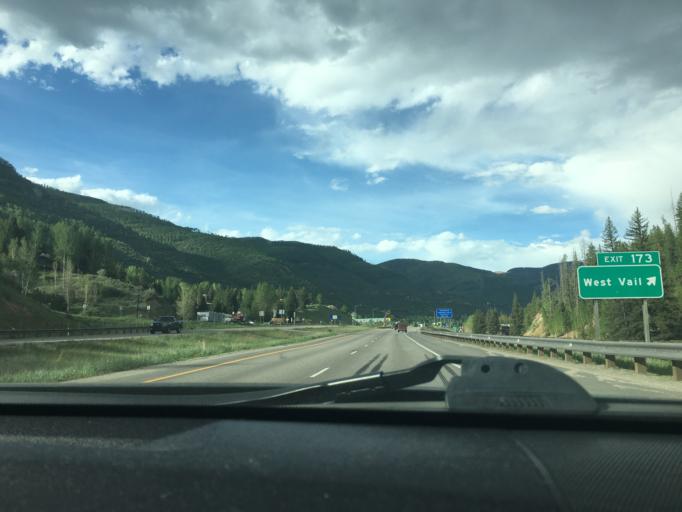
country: US
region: Colorado
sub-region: Eagle County
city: Minturn
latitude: 39.6225
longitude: -106.4260
